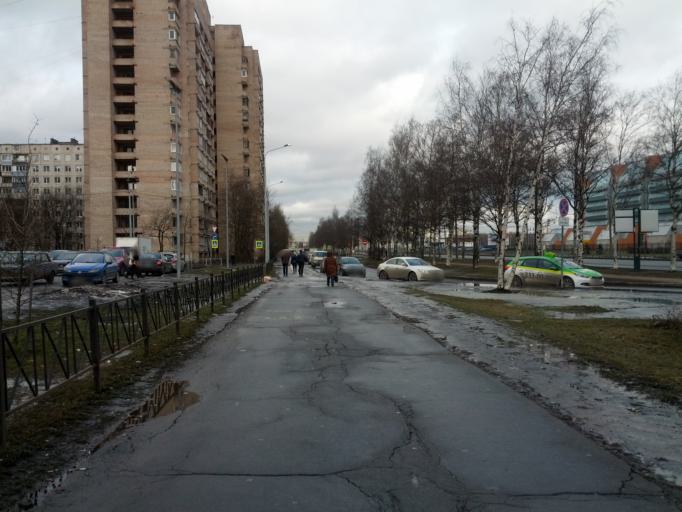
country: RU
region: Leningrad
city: Rybatskoye
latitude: 59.9006
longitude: 30.4876
